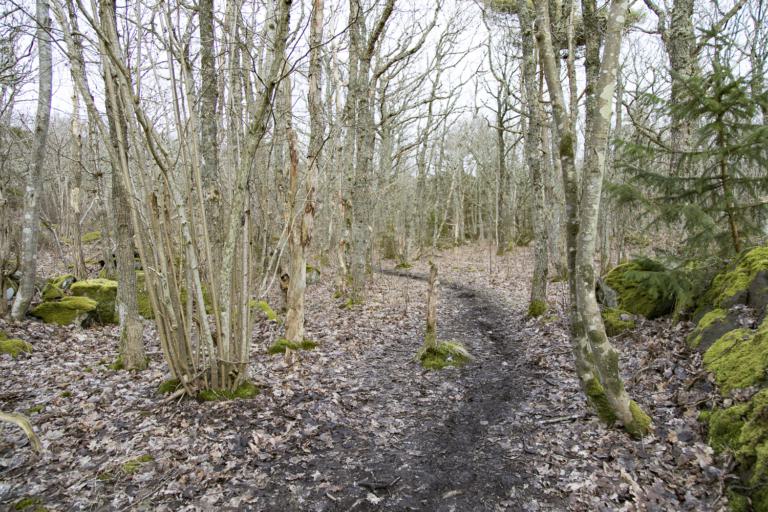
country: SE
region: Halland
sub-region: Varbergs Kommun
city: Varberg
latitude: 57.0853
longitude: 12.2434
